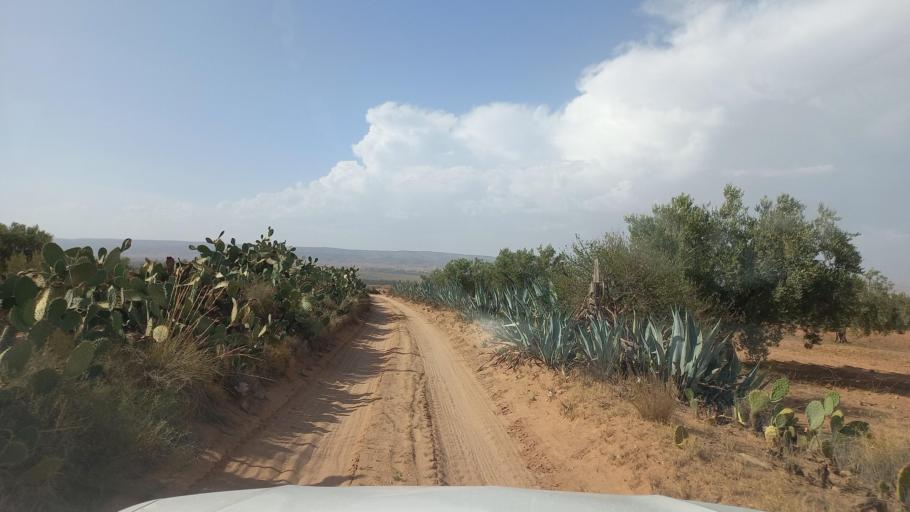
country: TN
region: Al Qasrayn
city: Kasserine
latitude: 35.2076
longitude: 8.9677
